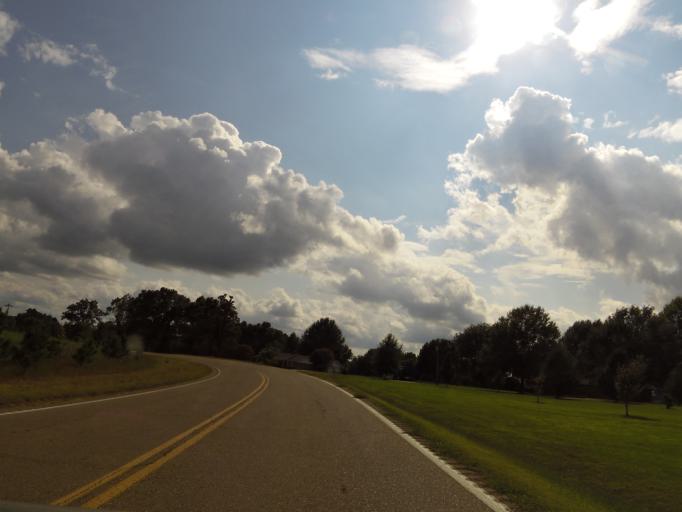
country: US
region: Mississippi
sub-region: Alcorn County
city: Farmington
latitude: 35.0462
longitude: -88.4461
